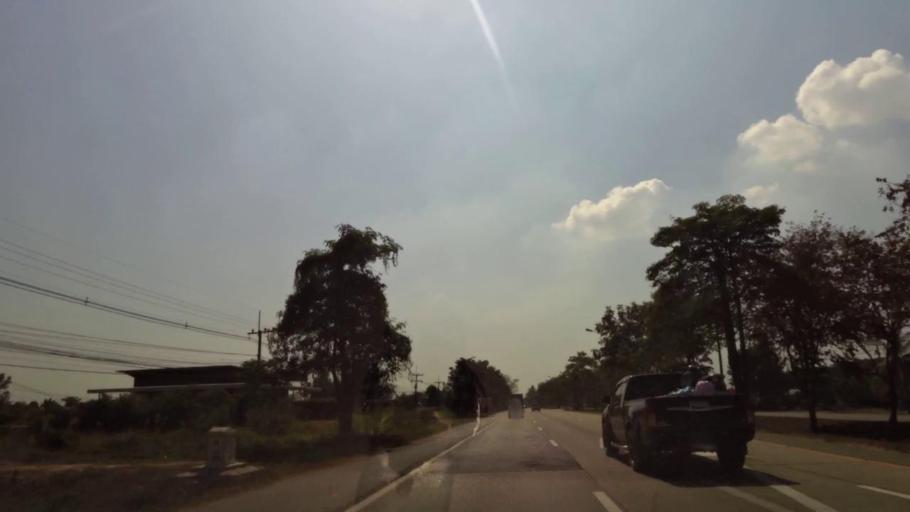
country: TH
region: Phichit
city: Wachira Barami
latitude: 16.5488
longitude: 100.1463
